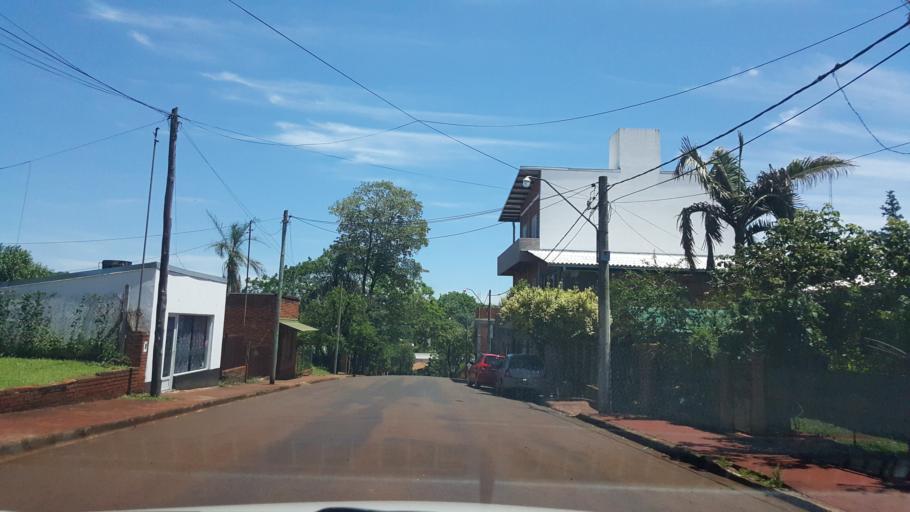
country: AR
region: Misiones
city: Capiovi
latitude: -26.9270
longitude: -55.0582
